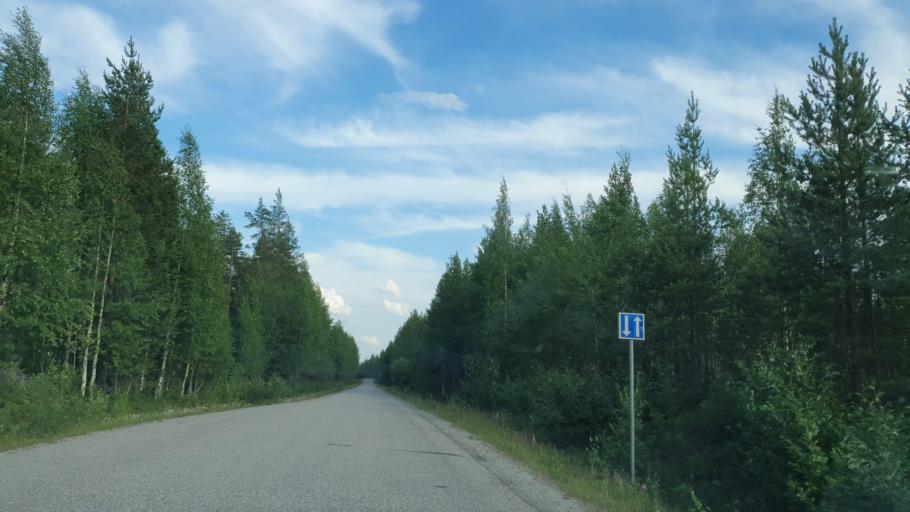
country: FI
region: Kainuu
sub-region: Kehys-Kainuu
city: Kuhmo
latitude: 64.2854
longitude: 29.3863
